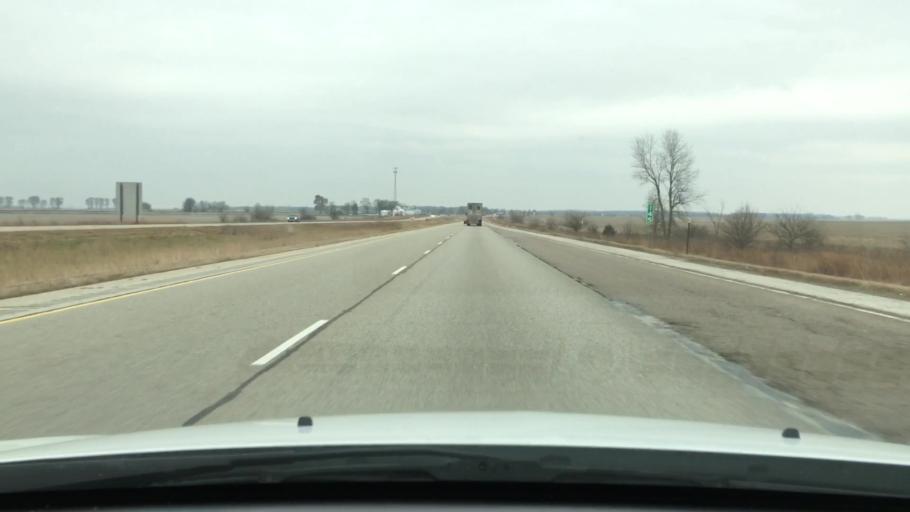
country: US
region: Illinois
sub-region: Logan County
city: Atlanta
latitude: 40.3159
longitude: -89.1598
